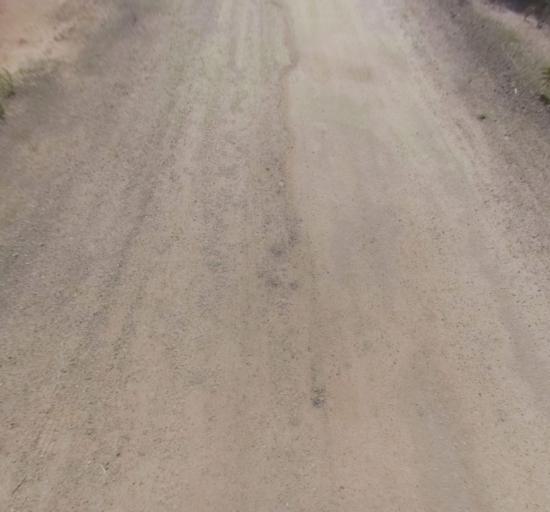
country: US
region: California
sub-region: Madera County
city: Chowchilla
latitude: 37.0109
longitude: -120.3608
